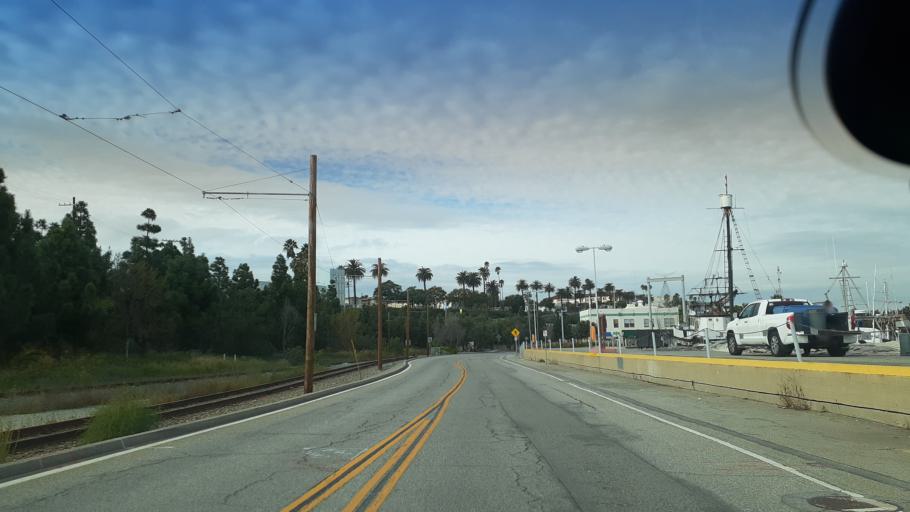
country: US
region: California
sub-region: Los Angeles County
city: San Pedro
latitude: 33.7307
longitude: -118.2783
